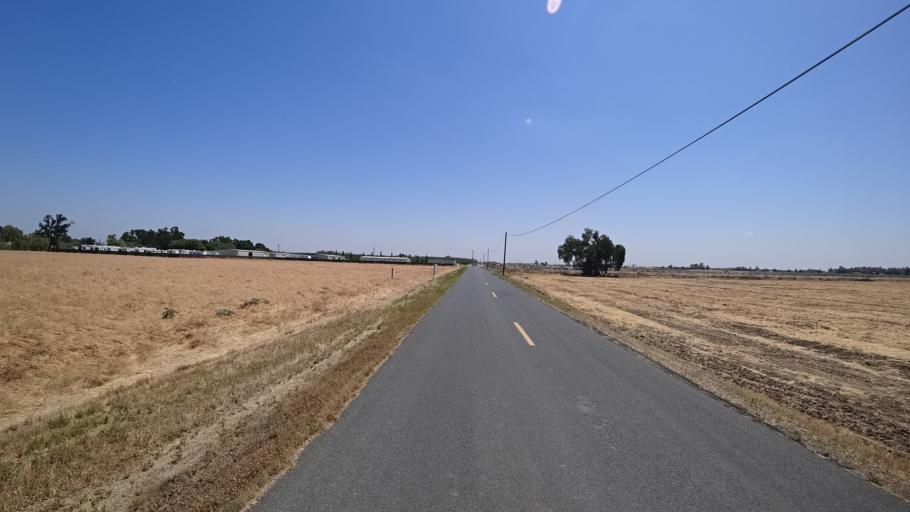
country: US
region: California
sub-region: Kings County
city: Armona
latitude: 36.3057
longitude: -119.7049
